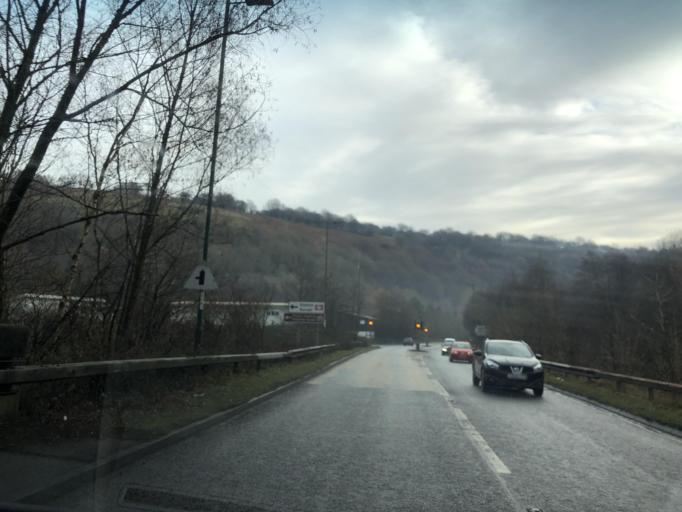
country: GB
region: Wales
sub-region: Caerphilly County Borough
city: Crumlin
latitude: 51.6978
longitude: -3.1318
